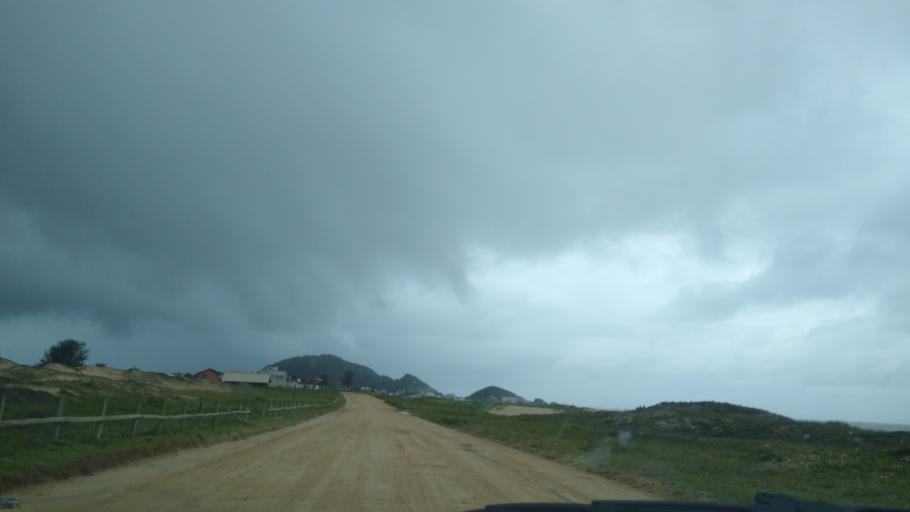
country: BR
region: Santa Catarina
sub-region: Sao Francisco Do Sul
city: Sao Francisco do Sul
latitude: -26.2426
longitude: -48.5082
